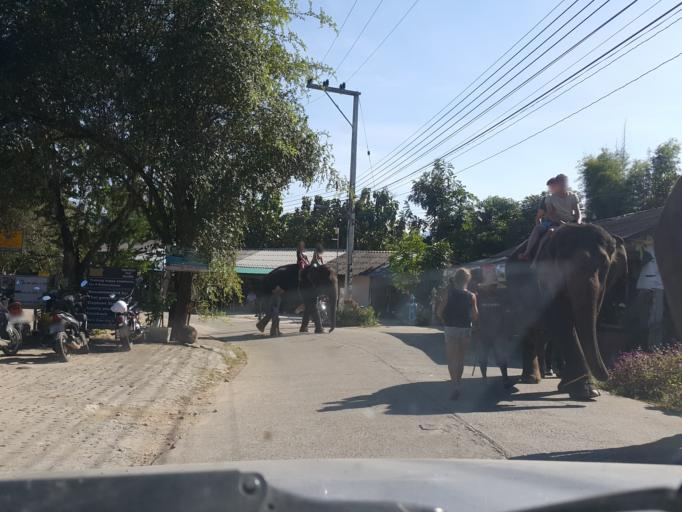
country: TH
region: Mae Hong Son
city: Mae Hi
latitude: 19.3107
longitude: 98.4630
